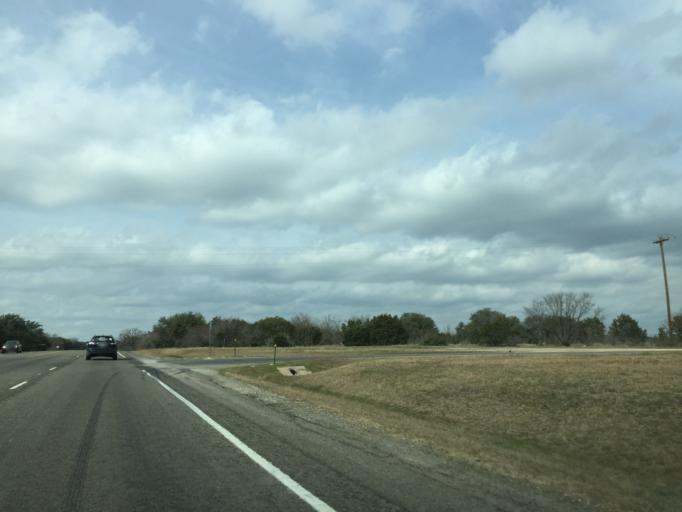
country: US
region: Texas
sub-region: Burnet County
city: Meadowlakes
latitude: 30.4998
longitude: -98.2668
